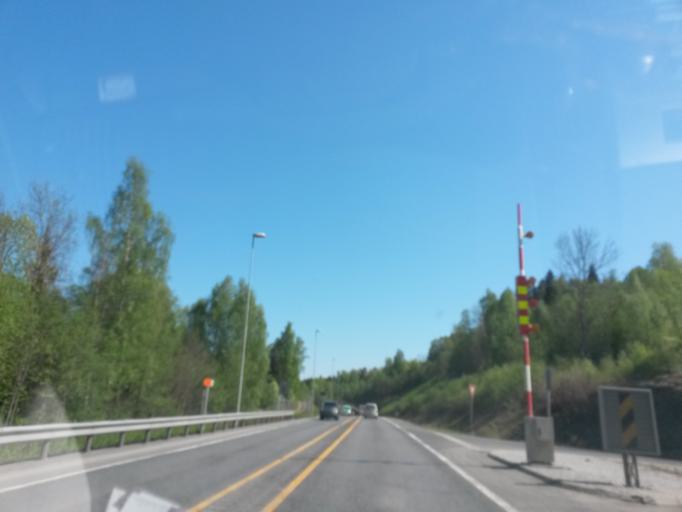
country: NO
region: Buskerud
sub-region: Drammen
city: Drammen
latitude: 59.7388
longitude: 10.1521
